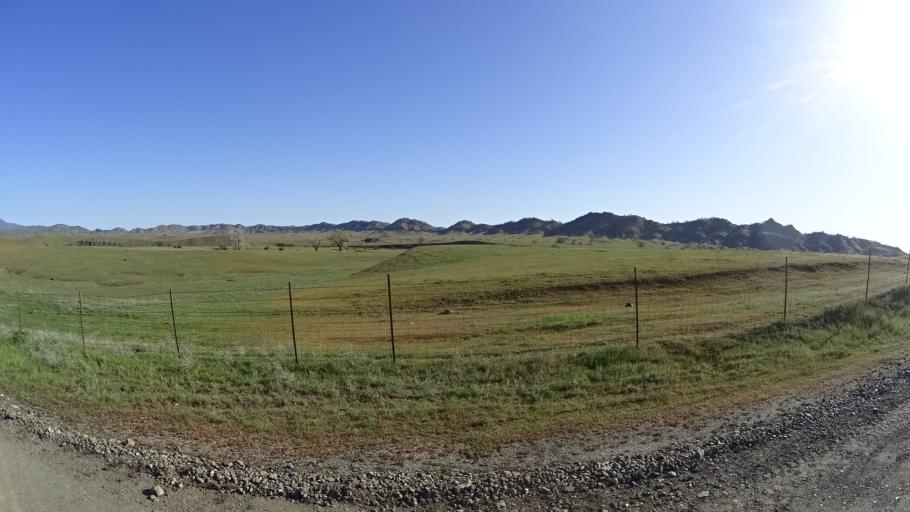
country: US
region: California
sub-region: Tehama County
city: Rancho Tehama Reserve
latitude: 39.7969
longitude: -122.5506
